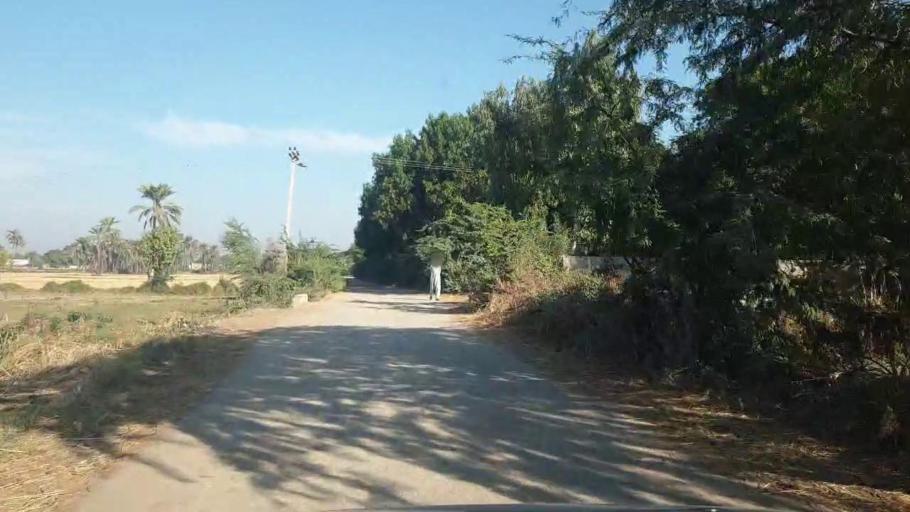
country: PK
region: Sindh
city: Talhar
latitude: 24.8933
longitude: 68.8128
